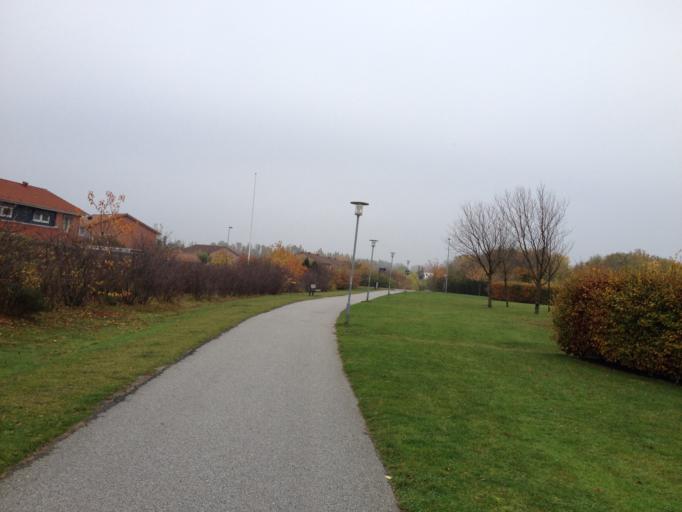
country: SE
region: Skane
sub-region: Burlovs Kommun
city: Arloev
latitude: 55.6065
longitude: 13.0524
